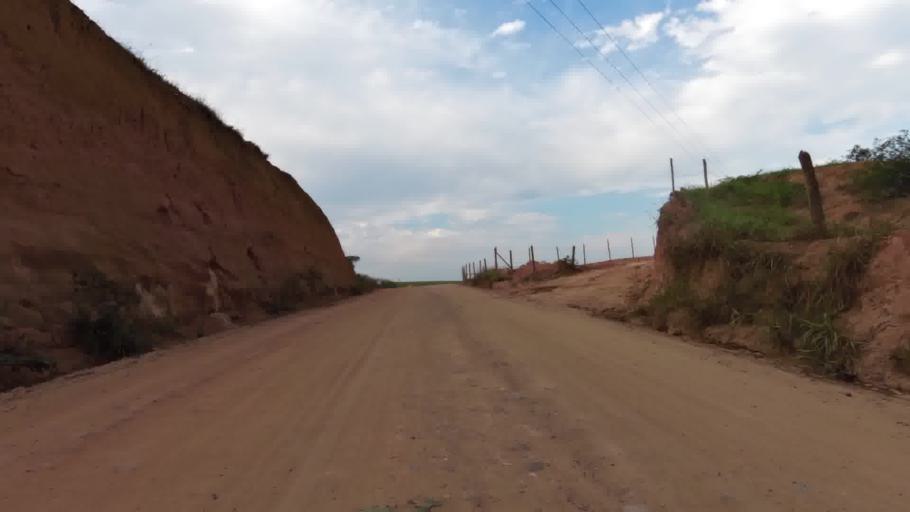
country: BR
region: Espirito Santo
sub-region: Piuma
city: Piuma
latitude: -20.8351
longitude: -40.7433
